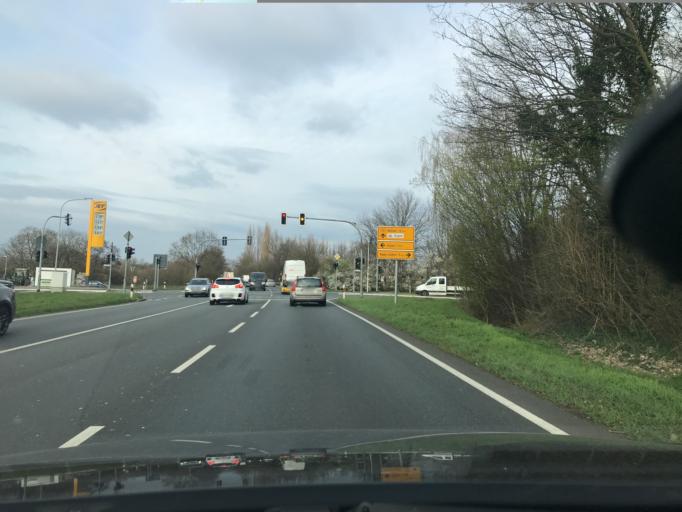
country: DE
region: North Rhine-Westphalia
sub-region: Regierungsbezirk Dusseldorf
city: Alpen
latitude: 51.5709
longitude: 6.5214
